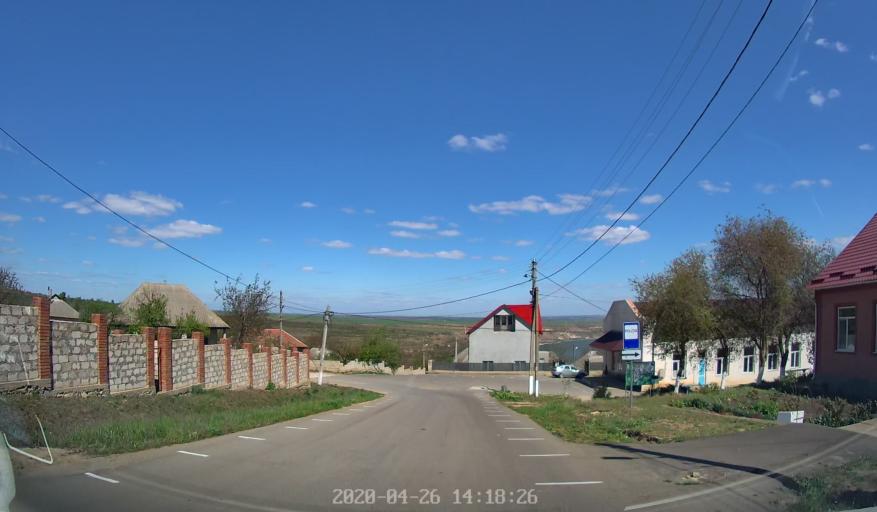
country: MD
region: Telenesti
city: Cocieri
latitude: 47.3549
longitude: 29.0593
